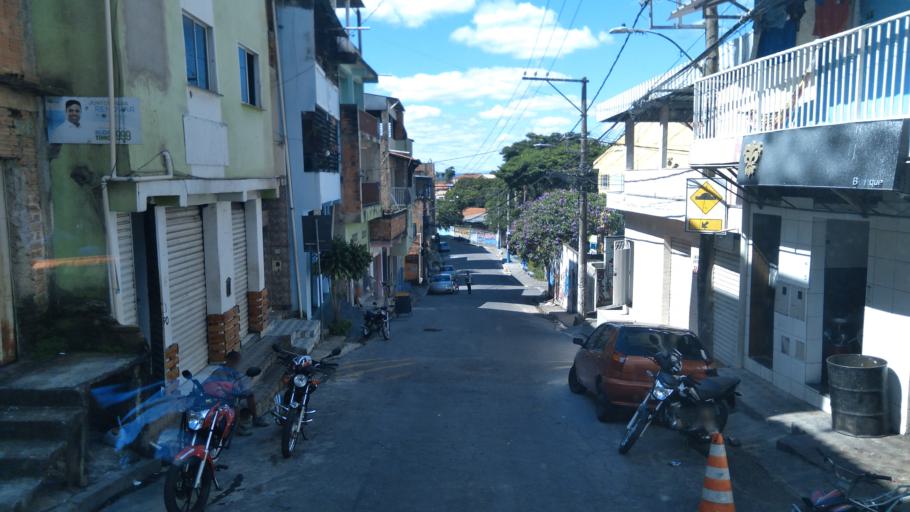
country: BR
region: Minas Gerais
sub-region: Belo Horizonte
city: Belo Horizonte
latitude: -19.8530
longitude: -43.8859
